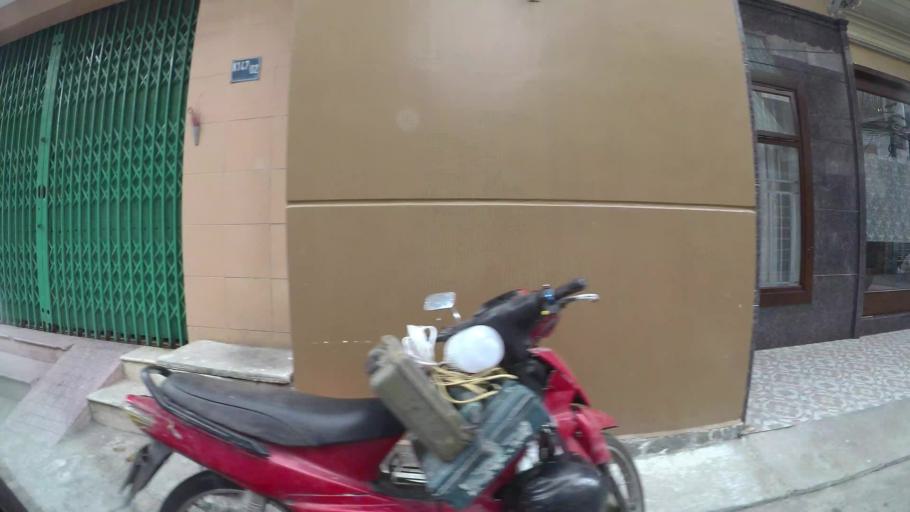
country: VN
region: Da Nang
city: Da Nang
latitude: 16.0556
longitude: 108.2098
